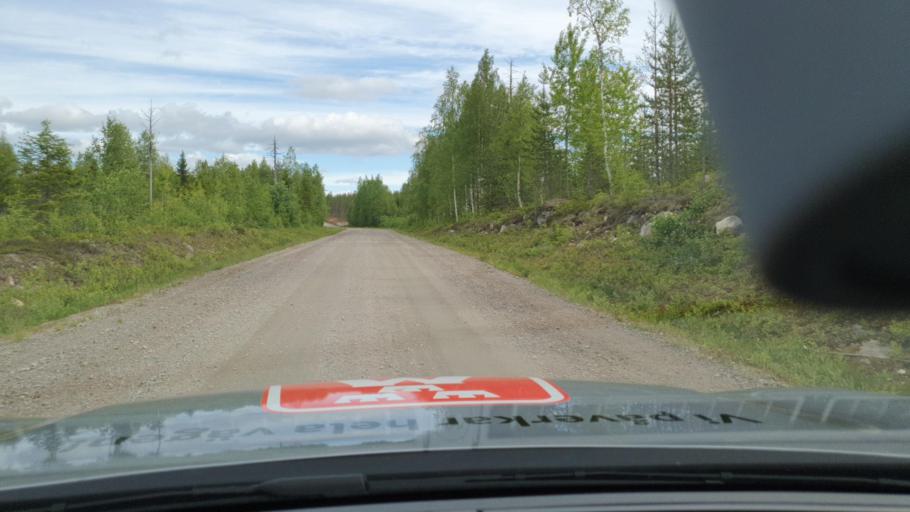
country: SE
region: Norrbotten
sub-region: Kalix Kommun
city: Rolfs
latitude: 65.9034
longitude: 23.1039
